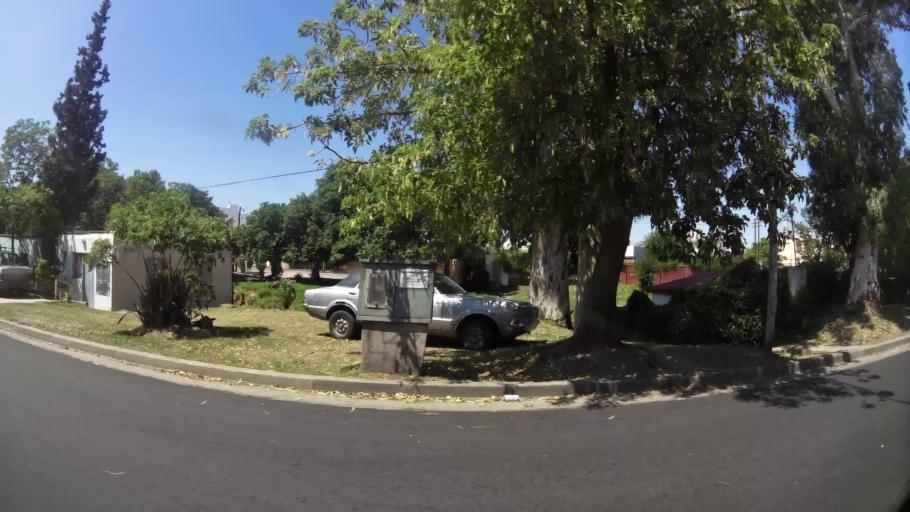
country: AR
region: Cordoba
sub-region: Departamento de Capital
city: Cordoba
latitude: -31.4007
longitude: -64.1924
